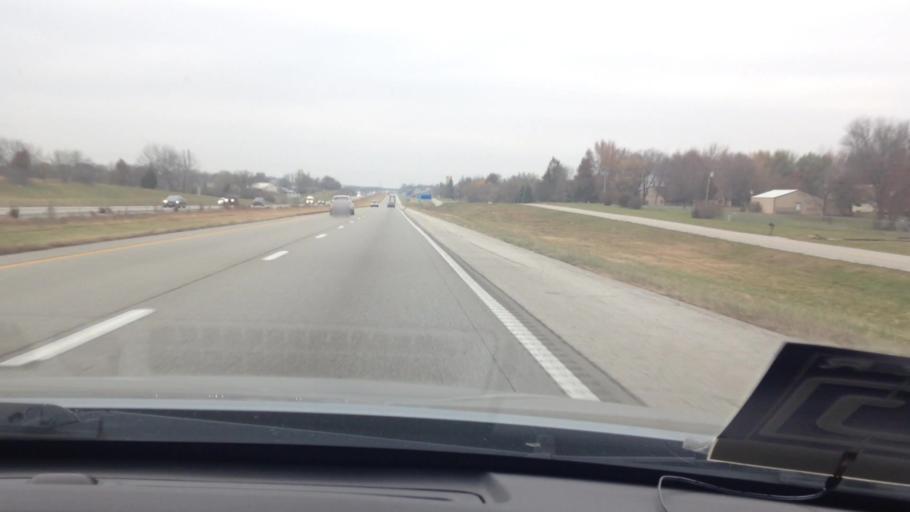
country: US
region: Missouri
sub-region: Cass County
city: Peculiar
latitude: 38.7117
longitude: -94.4441
